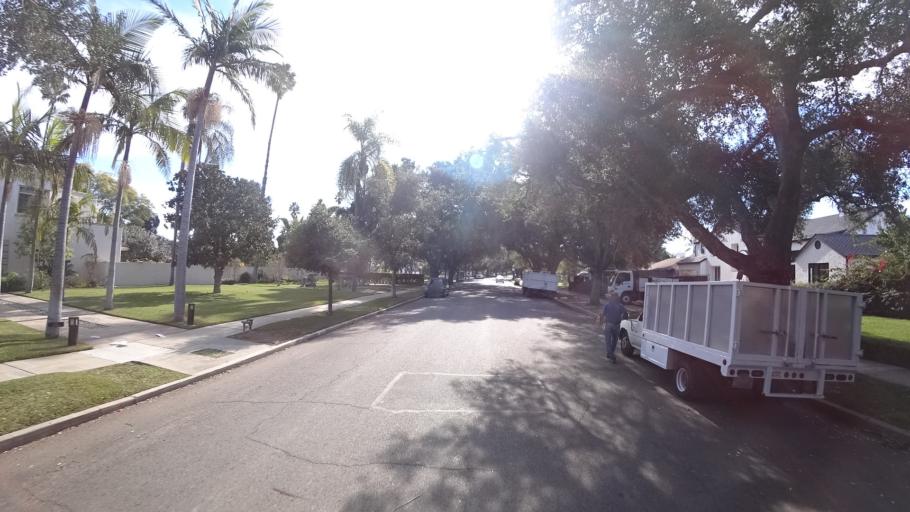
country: US
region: California
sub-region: Orange County
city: Santa Ana
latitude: 33.7667
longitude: -117.8751
